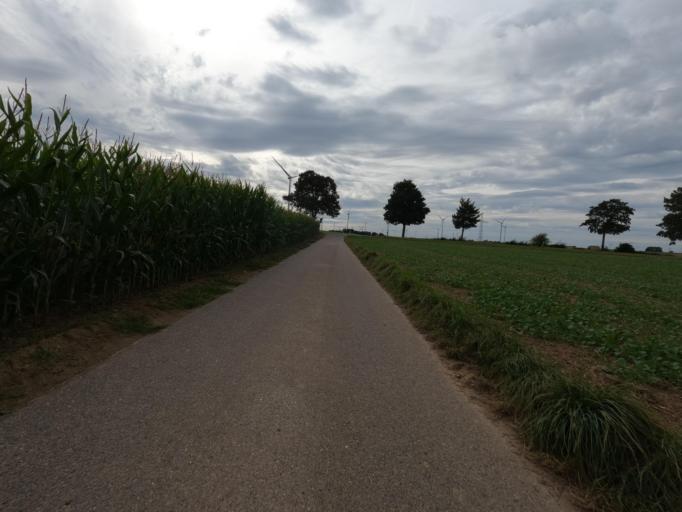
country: DE
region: North Rhine-Westphalia
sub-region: Regierungsbezirk Koln
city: Linnich
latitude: 50.9932
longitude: 6.2554
